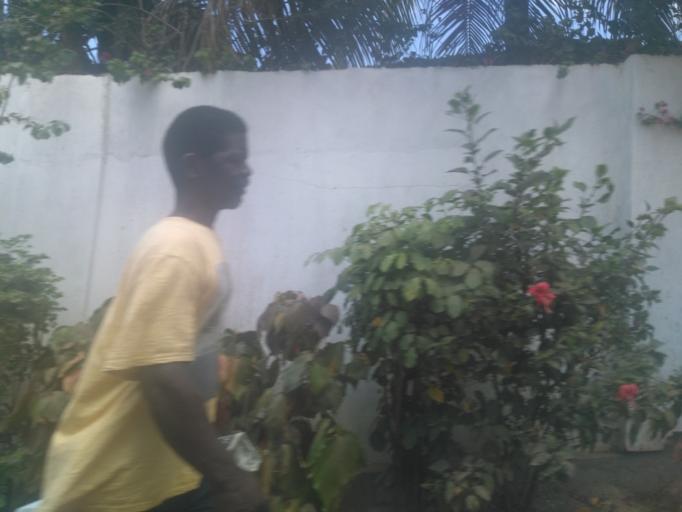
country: TZ
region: Zanzibar Urban/West
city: Zanzibar
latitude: -6.2179
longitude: 39.2184
